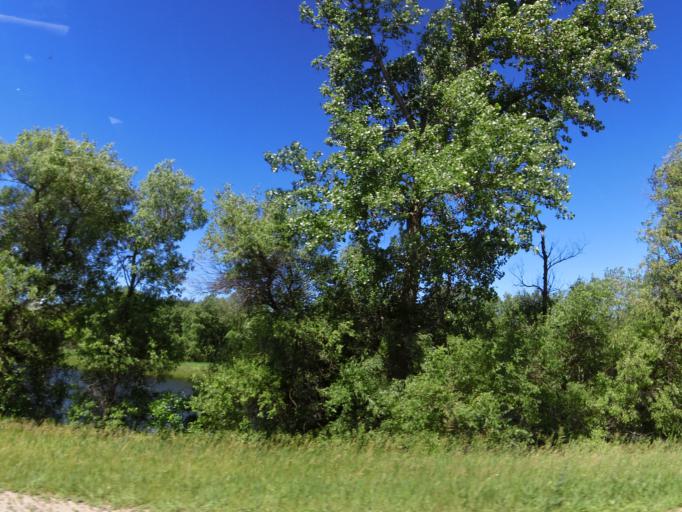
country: US
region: Minnesota
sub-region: Polk County
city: Fosston
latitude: 47.6551
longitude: -95.9832
